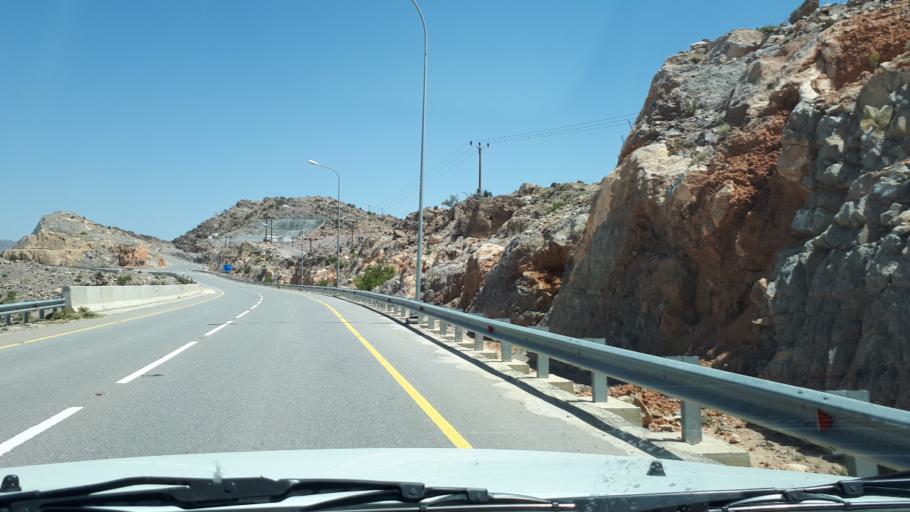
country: OM
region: Muhafazat ad Dakhiliyah
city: Izki
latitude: 23.0557
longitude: 57.7285
